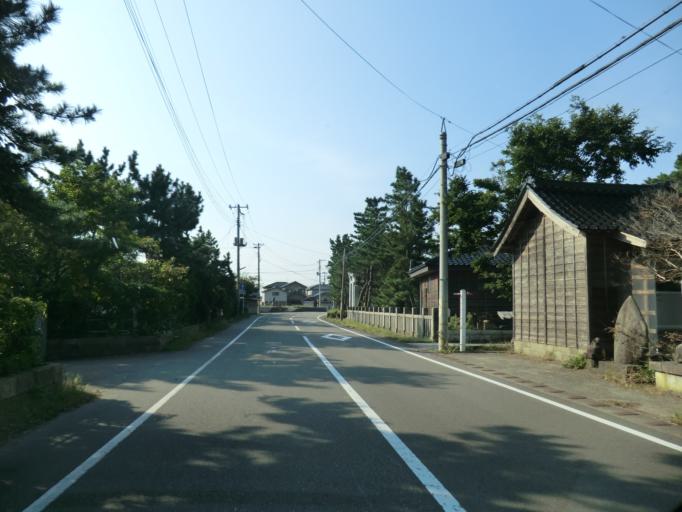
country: JP
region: Niigata
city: Kashiwazaki
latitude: 37.4120
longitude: 138.5846
